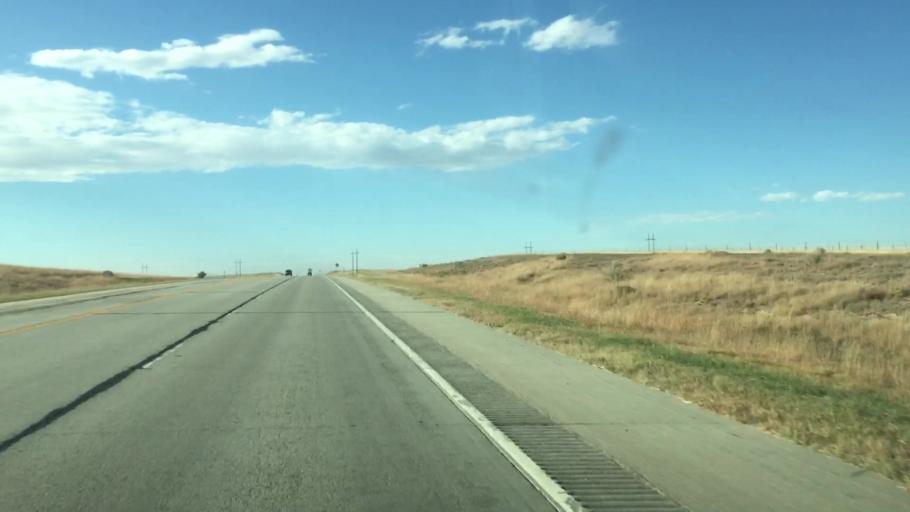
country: US
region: Colorado
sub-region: Lincoln County
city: Limon
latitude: 39.2446
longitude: -103.6291
